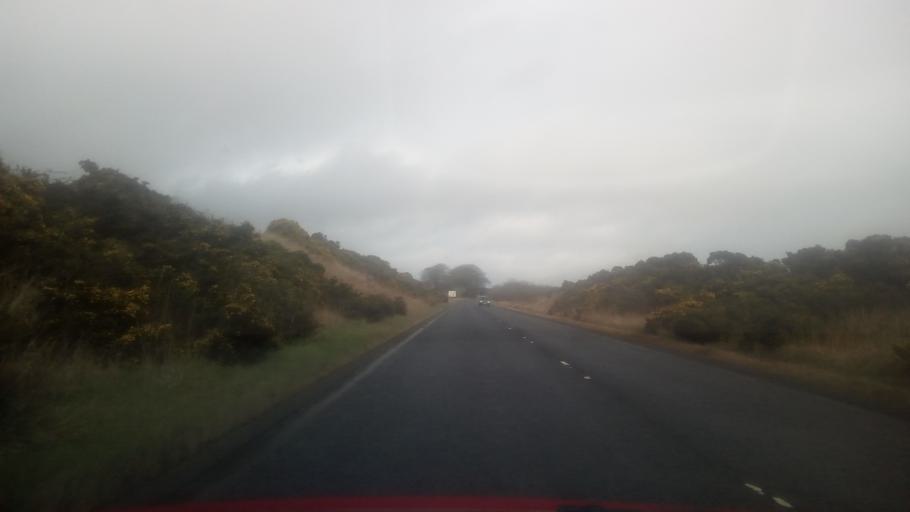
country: GB
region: Scotland
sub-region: The Scottish Borders
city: Duns
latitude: 55.7497
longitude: -2.4072
